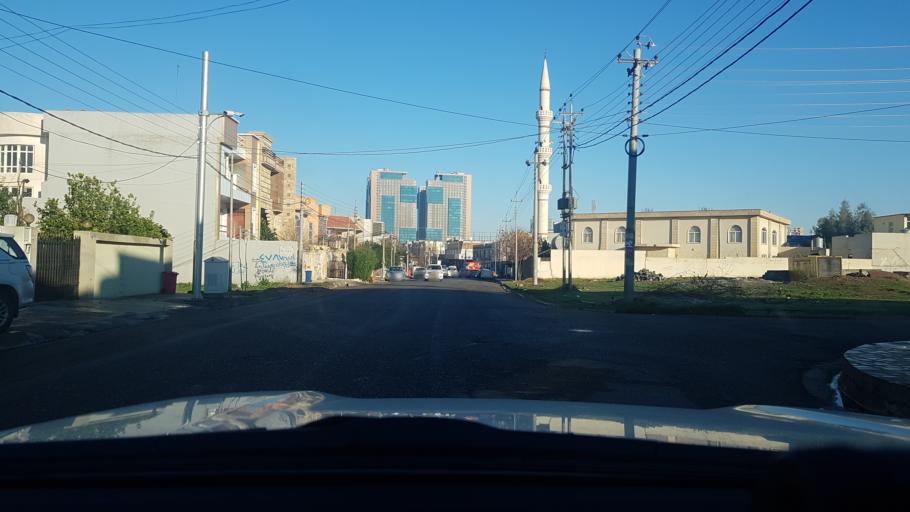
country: IQ
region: Arbil
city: Erbil
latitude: 36.2084
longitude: 44.0066
